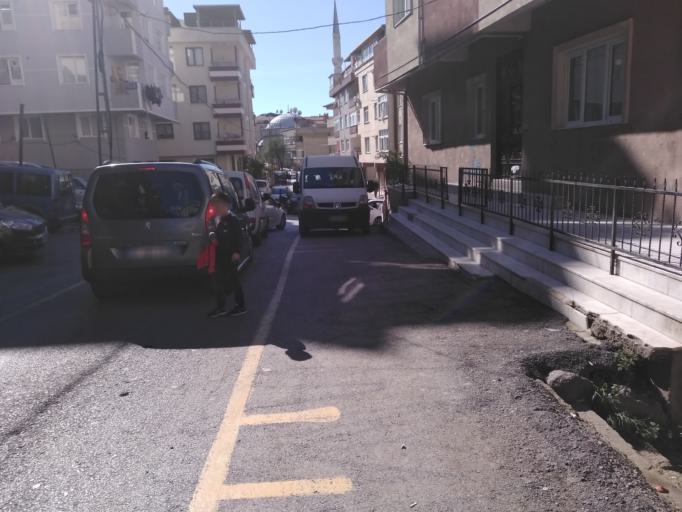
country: TR
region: Istanbul
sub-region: Atasehir
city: Atasehir
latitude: 40.9708
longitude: 29.1242
